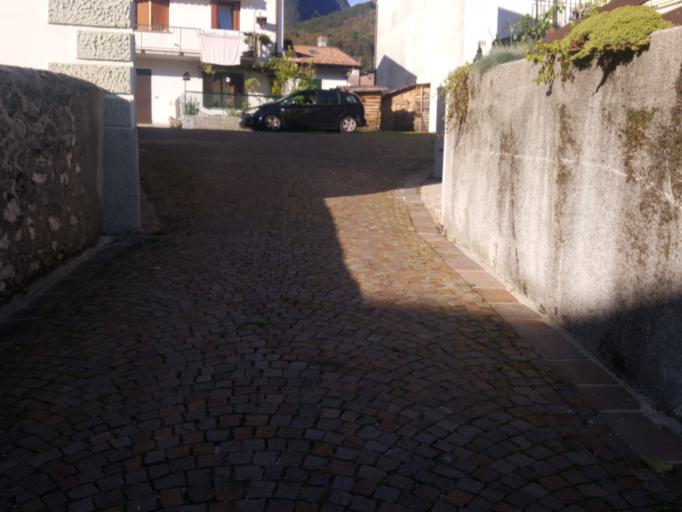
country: IT
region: Friuli Venezia Giulia
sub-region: Provincia di Udine
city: Moggio di Sotto
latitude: 46.4064
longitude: 13.1907
